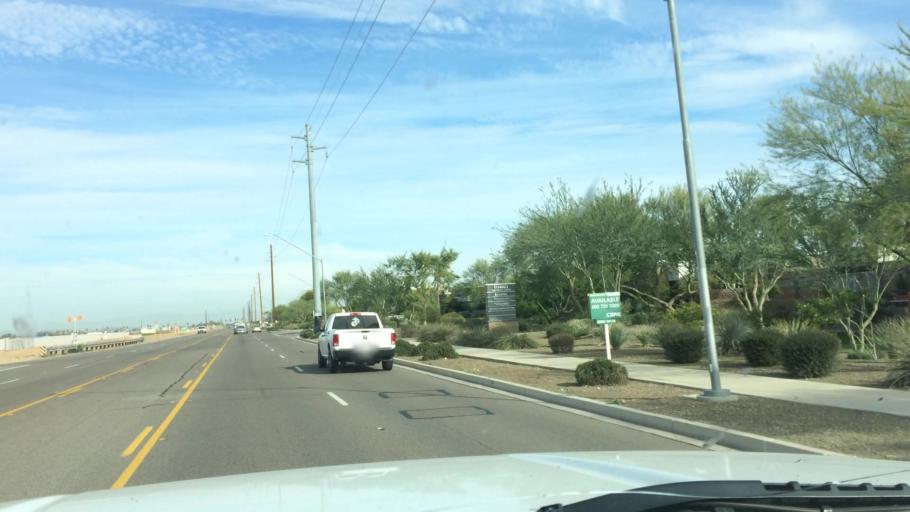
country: US
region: Arizona
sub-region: Maricopa County
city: Tolleson
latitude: 33.5126
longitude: -112.2724
